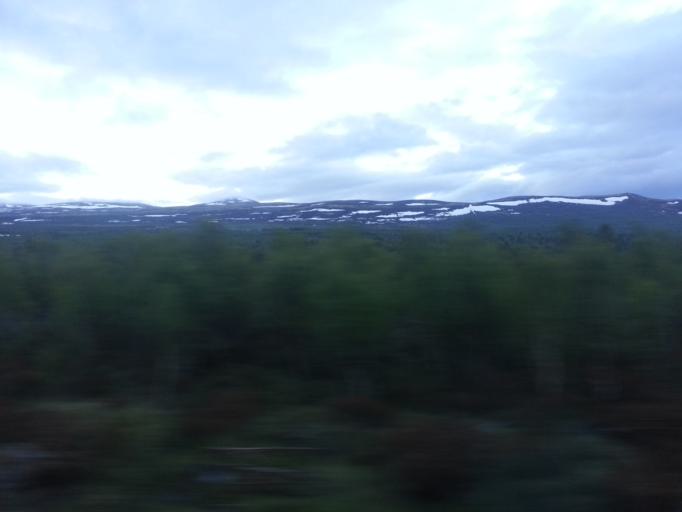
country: NO
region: Oppland
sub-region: Dovre
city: Dombas
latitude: 62.0994
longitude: 9.1941
